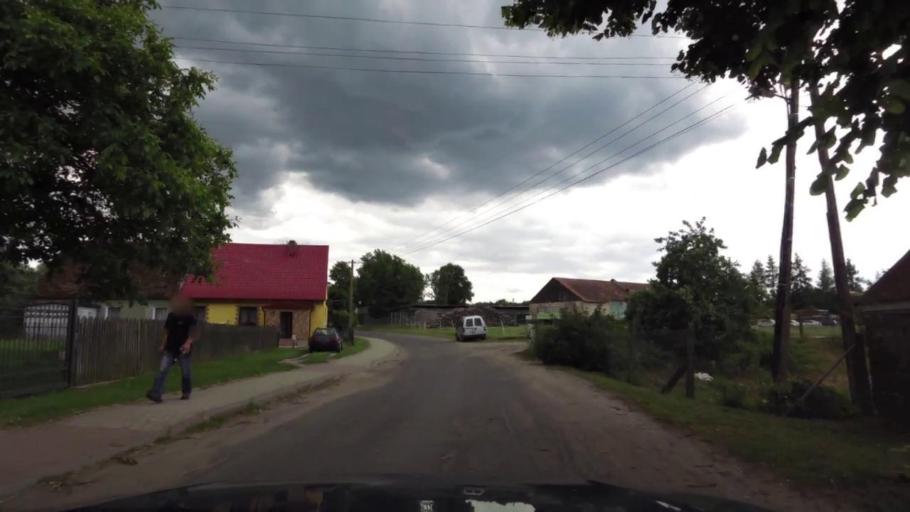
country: PL
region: West Pomeranian Voivodeship
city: Trzcinsko Zdroj
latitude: 52.9114
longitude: 14.5963
